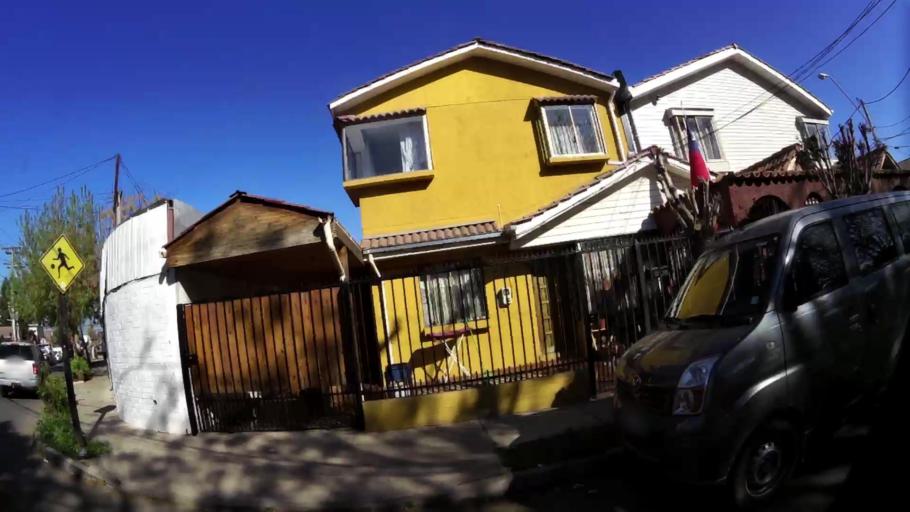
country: CL
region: Santiago Metropolitan
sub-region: Provincia de Santiago
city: Lo Prado
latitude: -33.4885
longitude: -70.7791
